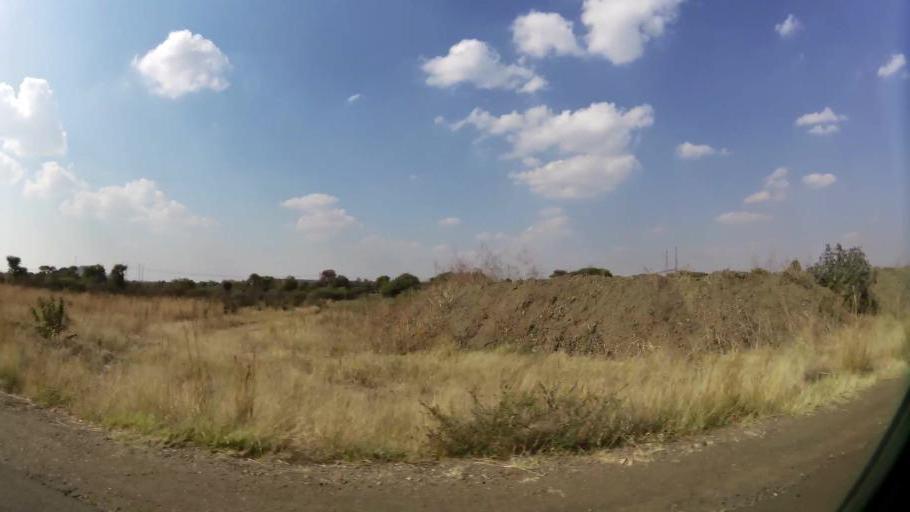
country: ZA
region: North-West
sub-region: Bojanala Platinum District Municipality
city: Mogwase
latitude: -25.4492
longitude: 27.0880
